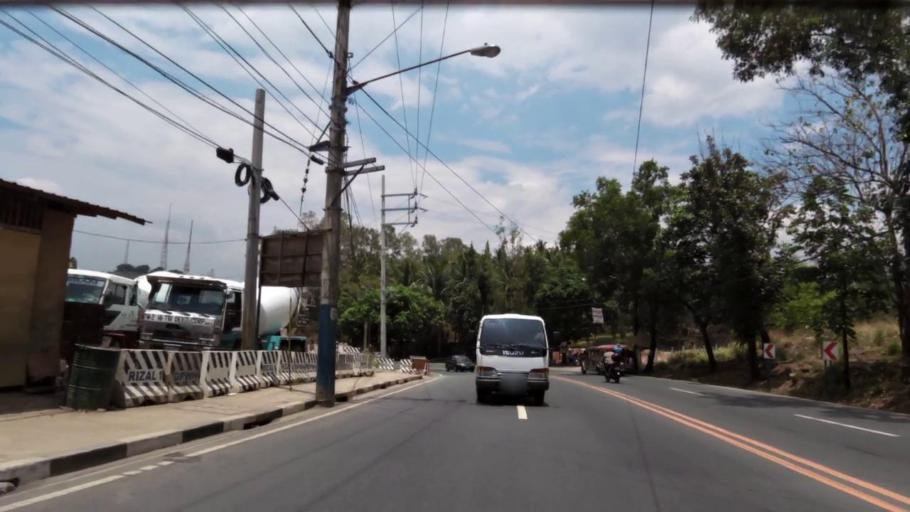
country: PH
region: Calabarzon
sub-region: Province of Rizal
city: Antipolo
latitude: 14.6085
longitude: 121.1638
